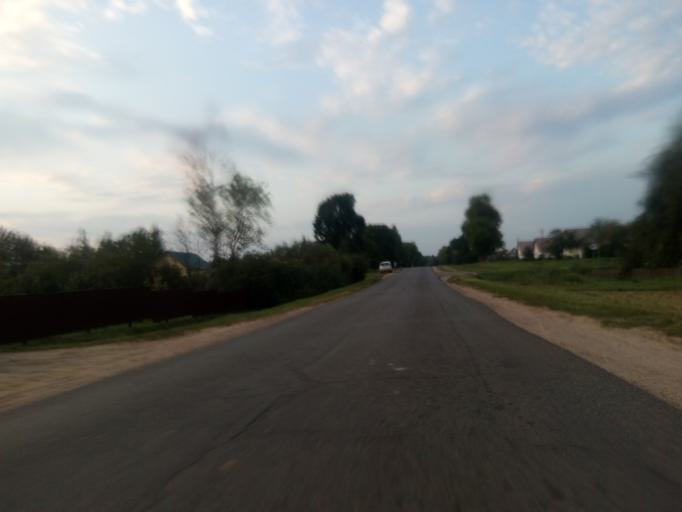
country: BY
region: Vitebsk
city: Dzisna
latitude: 55.6586
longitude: 28.3236
